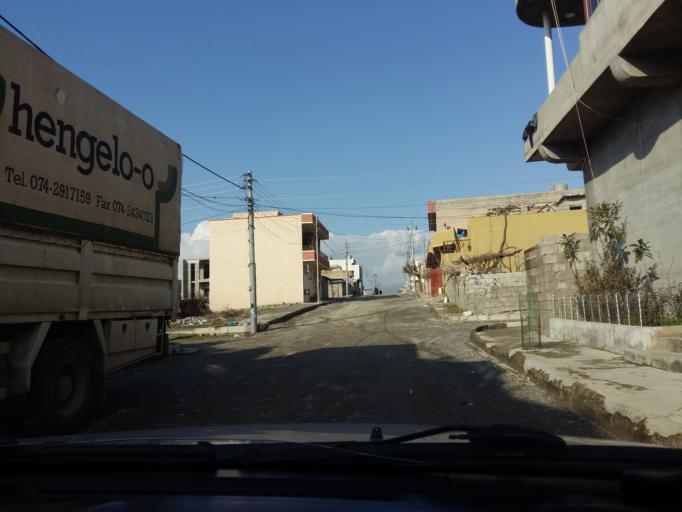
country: IQ
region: As Sulaymaniyah
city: Qeladize
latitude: 36.1754
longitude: 45.1376
